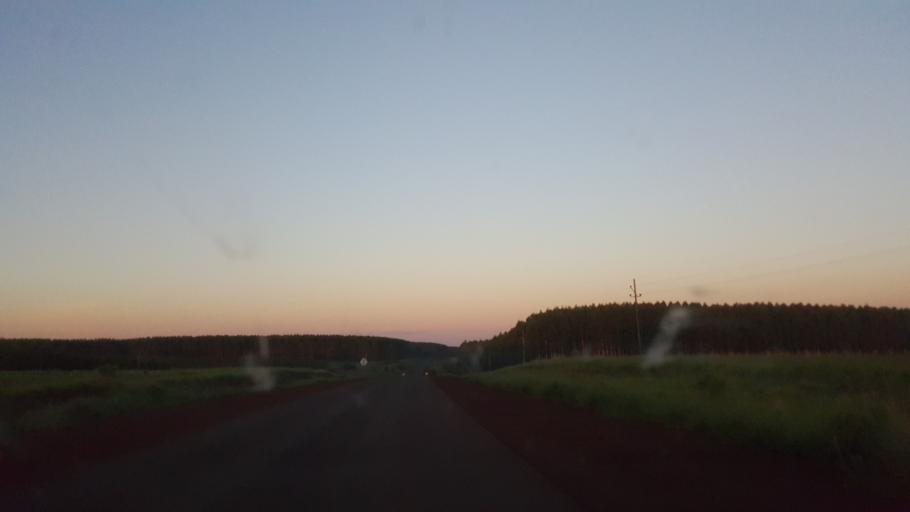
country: AR
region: Corrientes
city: Garruchos
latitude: -28.2602
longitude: -55.8585
